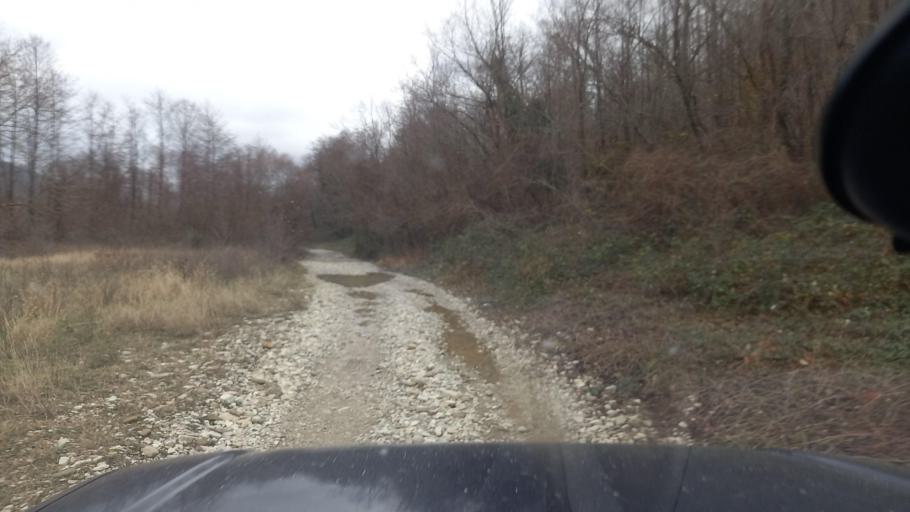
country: RU
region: Krasnodarskiy
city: Pshada
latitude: 44.4932
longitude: 38.4202
